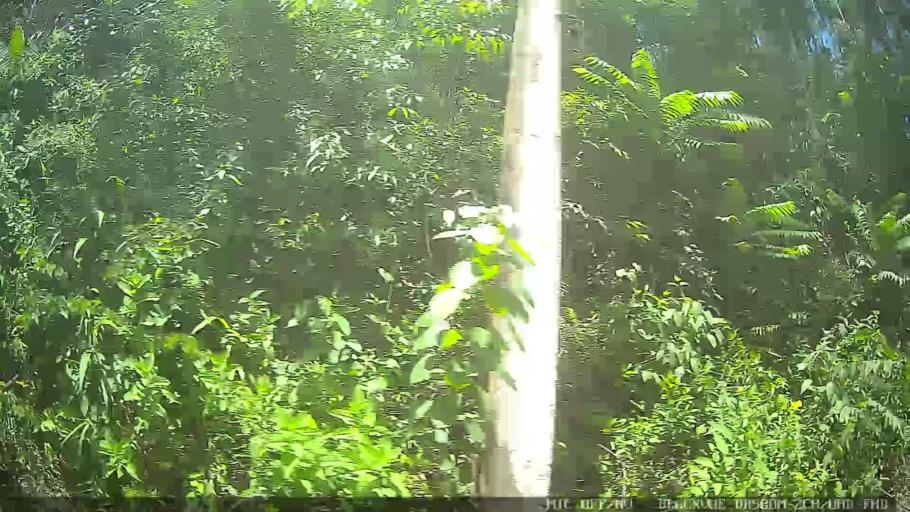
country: BR
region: Minas Gerais
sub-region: Extrema
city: Extrema
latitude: -22.8843
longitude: -46.2940
